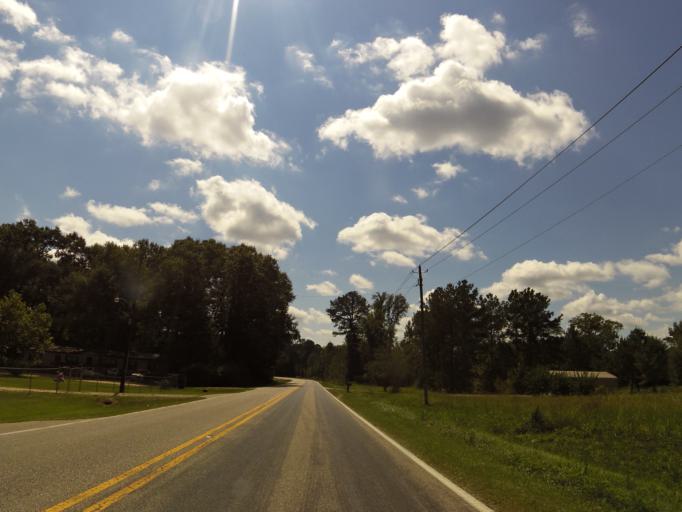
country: US
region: Alabama
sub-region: Dallas County
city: Selma
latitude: 32.3994
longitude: -87.0885
